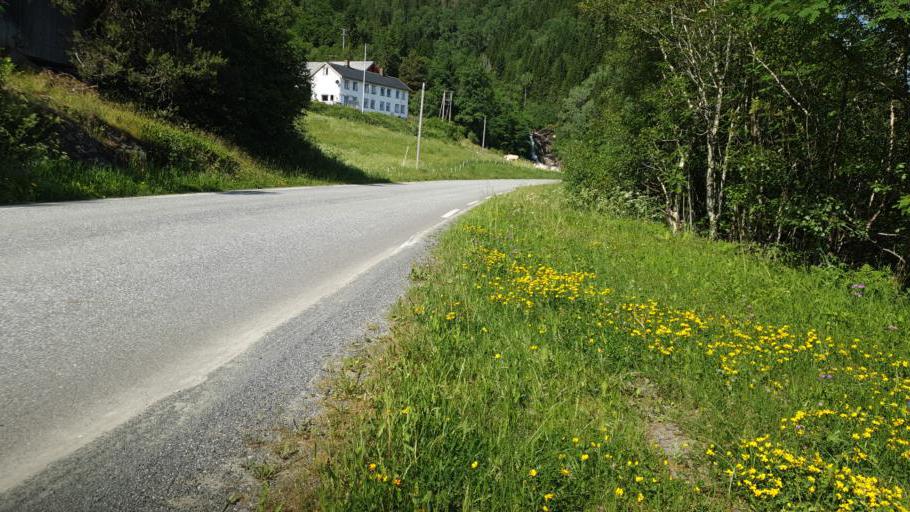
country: NO
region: Nord-Trondelag
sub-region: Leksvik
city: Leksvik
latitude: 63.6340
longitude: 10.5728
